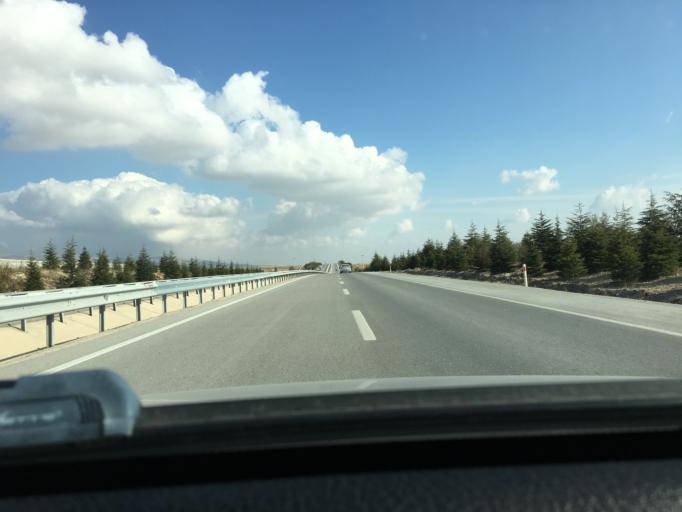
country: TR
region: Eskisehir
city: Kaymaz
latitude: 39.4855
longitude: 31.2832
